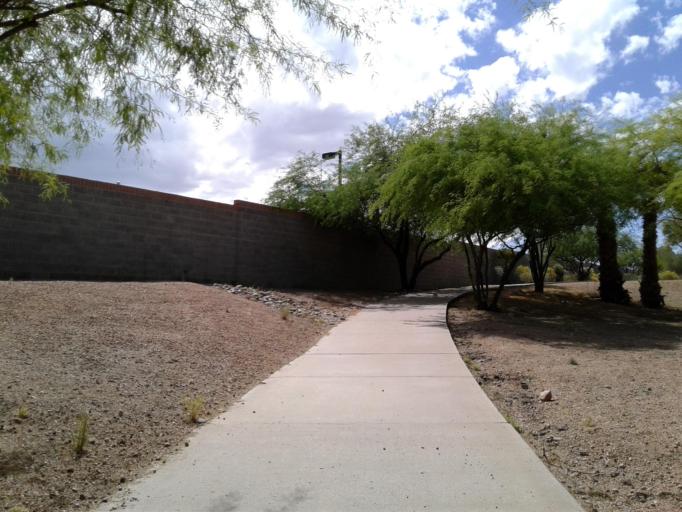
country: US
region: Arizona
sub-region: Maricopa County
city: Tempe Junction
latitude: 33.4681
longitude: -111.9412
